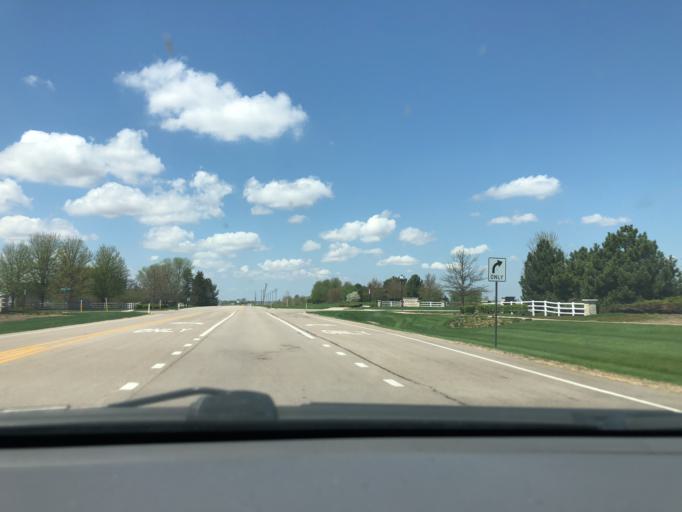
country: US
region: Illinois
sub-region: Kane County
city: Hampshire
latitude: 42.1064
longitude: -88.5376
